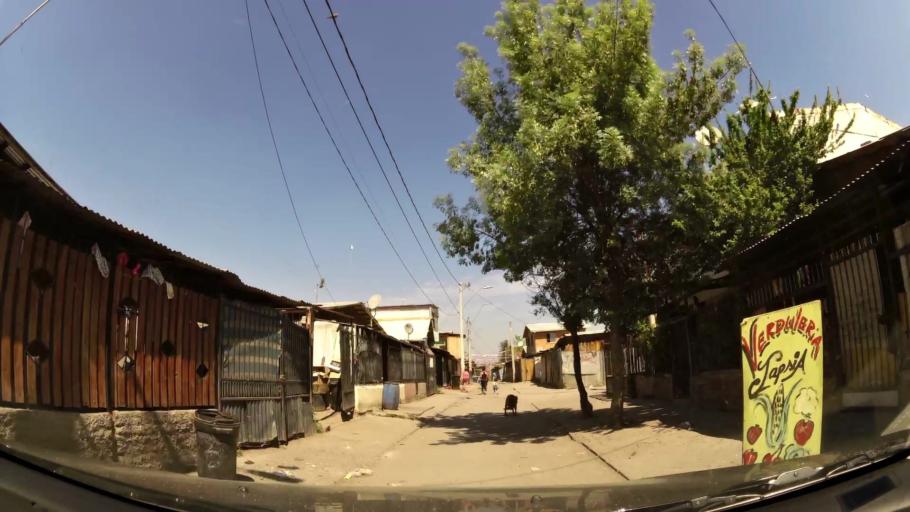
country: CL
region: Santiago Metropolitan
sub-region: Provincia de Santiago
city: La Pintana
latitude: -33.5922
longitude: -70.6097
